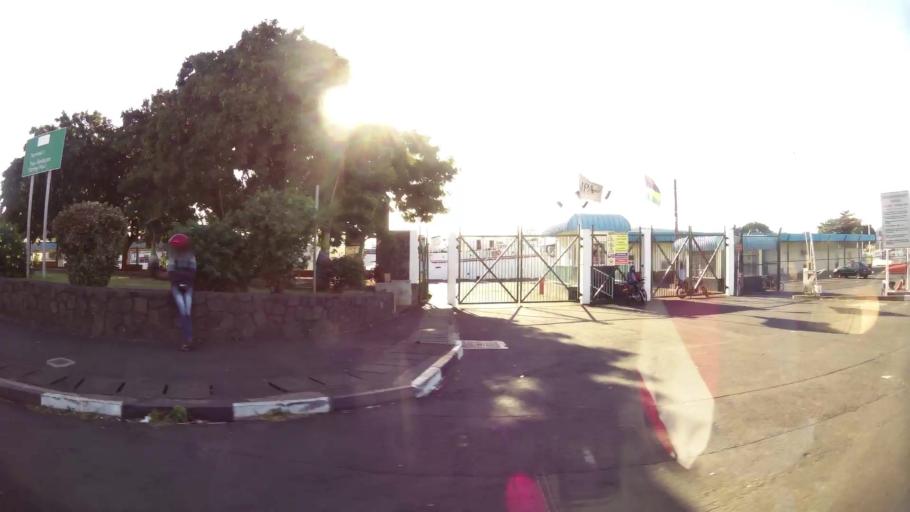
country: MU
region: Port Louis
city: Port Louis
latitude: -20.1580
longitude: 57.5042
